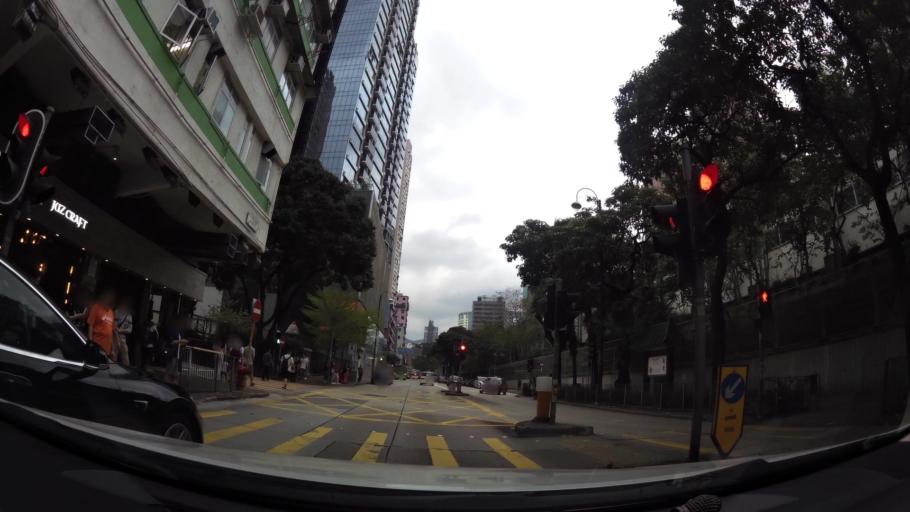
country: HK
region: Kowloon City
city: Kowloon
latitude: 22.3180
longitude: 114.1735
